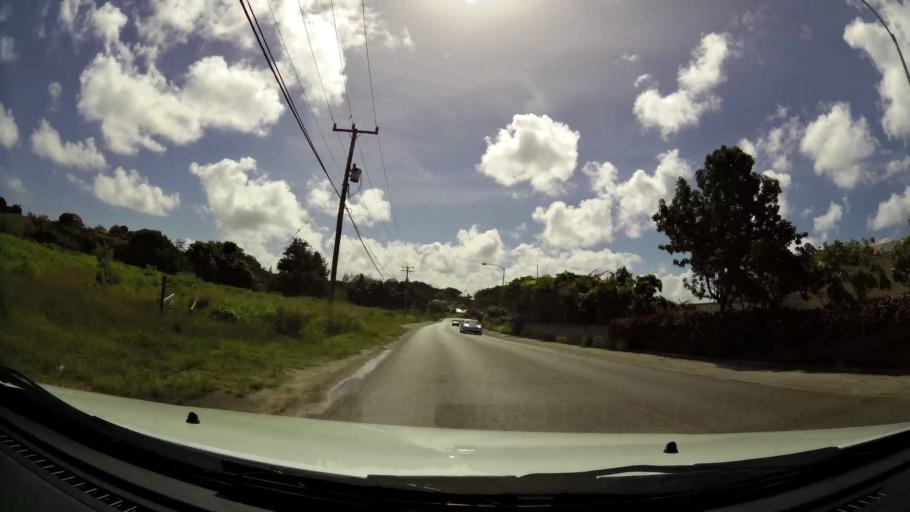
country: BB
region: Saint Peter
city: Speightstown
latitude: 13.2642
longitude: -59.6427
